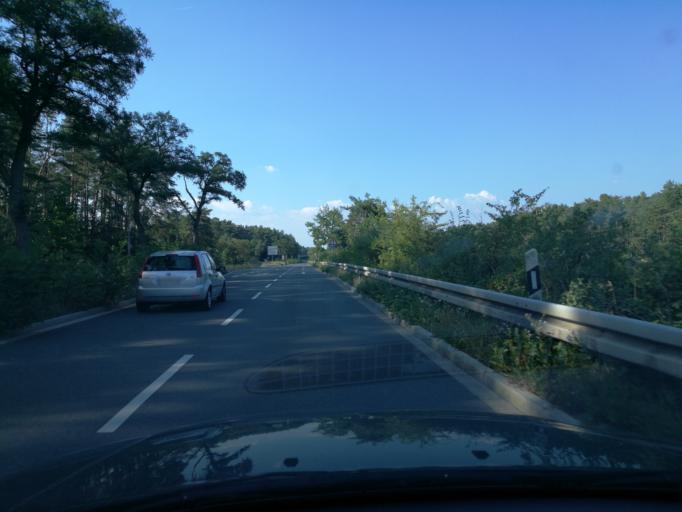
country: DE
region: Bavaria
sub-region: Regierungsbezirk Mittelfranken
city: Erlangen
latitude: 49.6043
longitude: 10.9717
